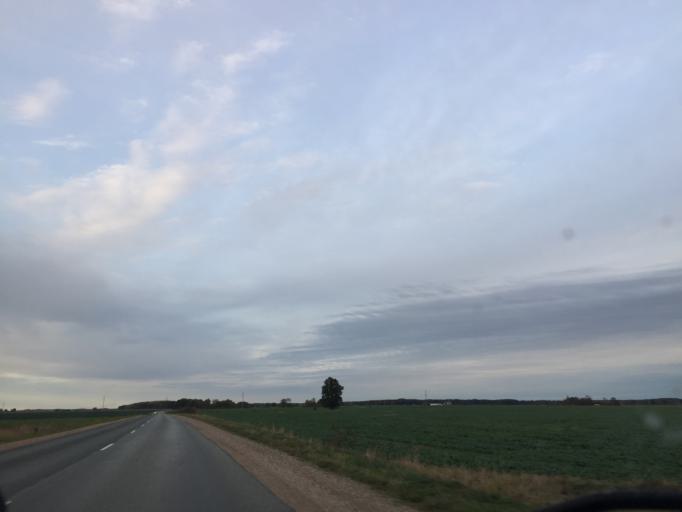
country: LV
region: Dobeles Rajons
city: Dobele
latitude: 56.6919
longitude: 23.3707
